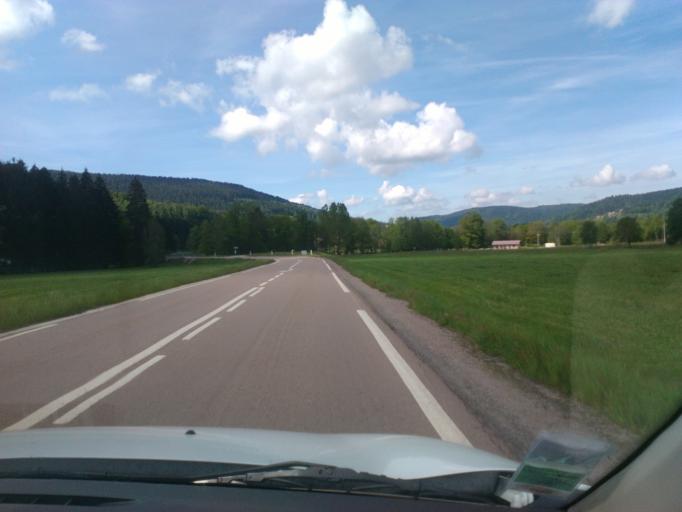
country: FR
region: Lorraine
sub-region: Departement des Vosges
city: Le Tholy
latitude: 48.0638
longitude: 6.7217
